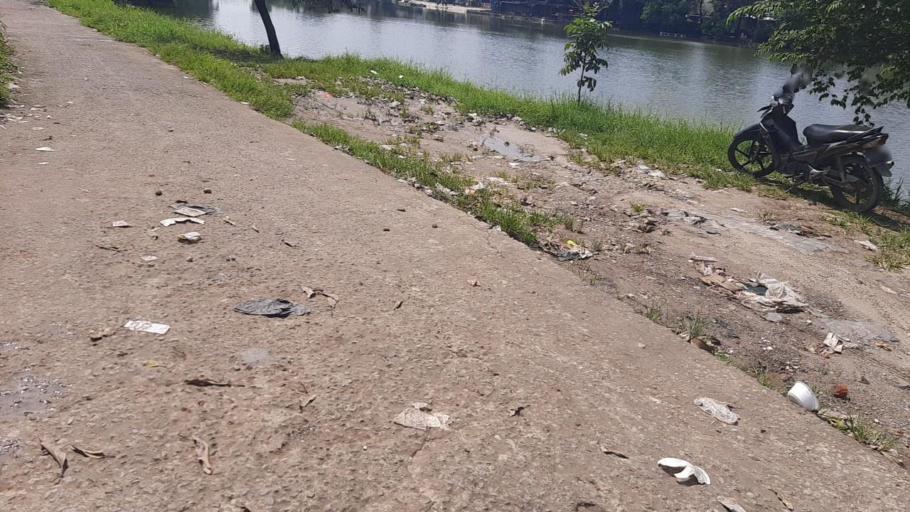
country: ID
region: West Java
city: Cileungsir
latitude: -6.4443
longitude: 106.9437
